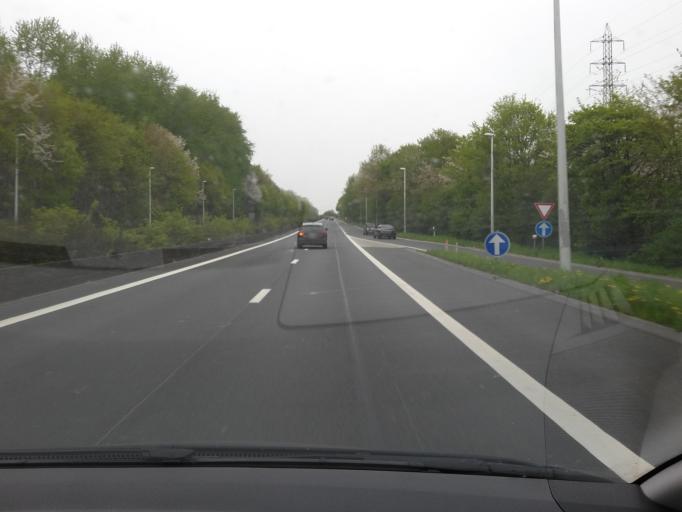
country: BE
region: Wallonia
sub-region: Province du Brabant Wallon
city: Mont-Saint-Guibert
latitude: 50.6429
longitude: 4.5901
